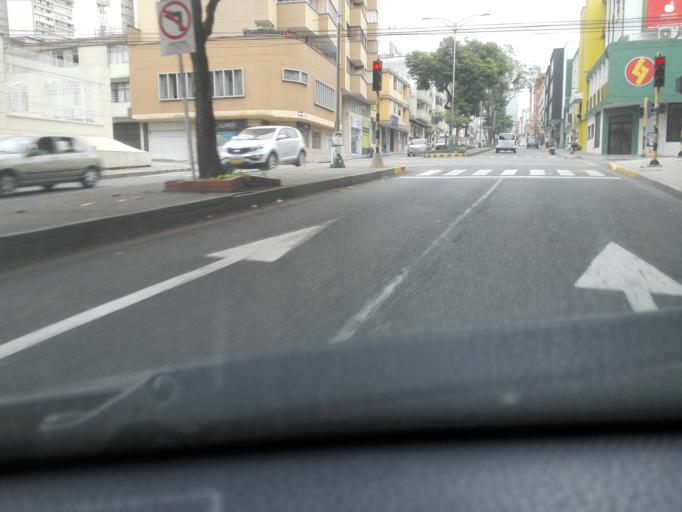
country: CO
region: Santander
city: Bucaramanga
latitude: 7.1195
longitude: -73.1218
